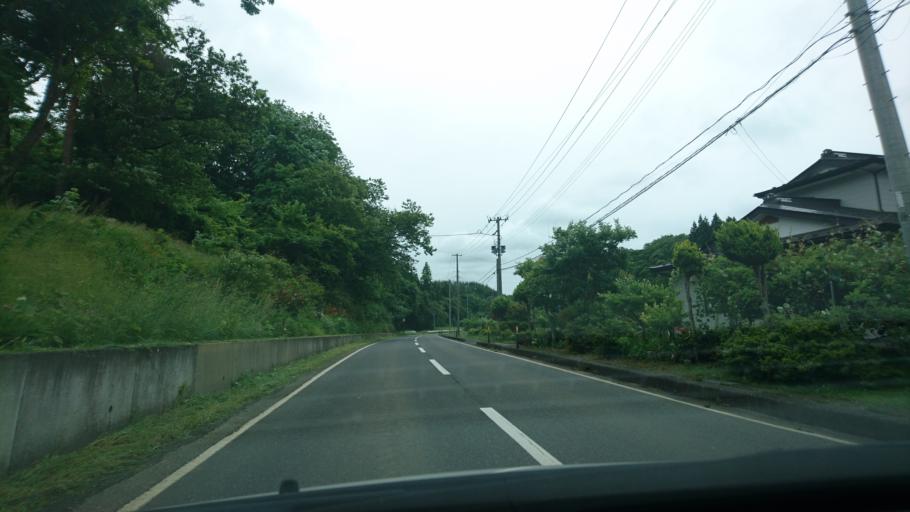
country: JP
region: Iwate
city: Ichinoseki
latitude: 38.9654
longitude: 141.0581
